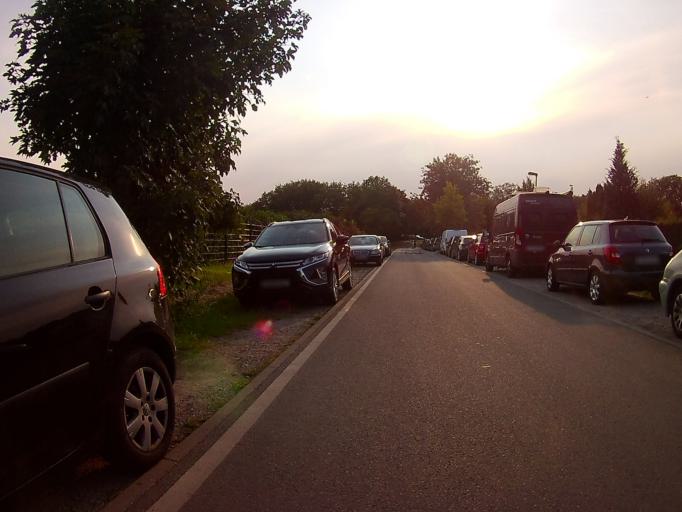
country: DE
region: Berlin
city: Weissensee
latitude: 52.5476
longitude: 13.4741
